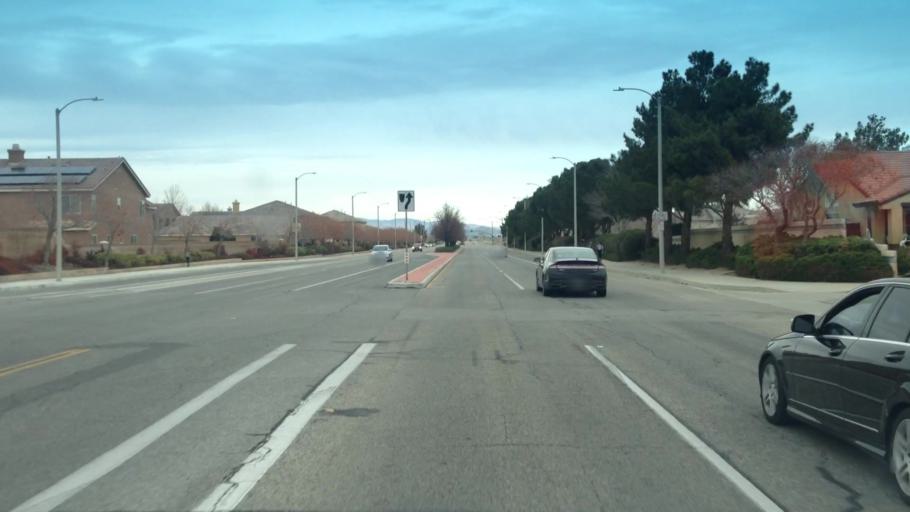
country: US
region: California
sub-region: Los Angeles County
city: Lancaster
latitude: 34.6934
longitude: -118.1838
